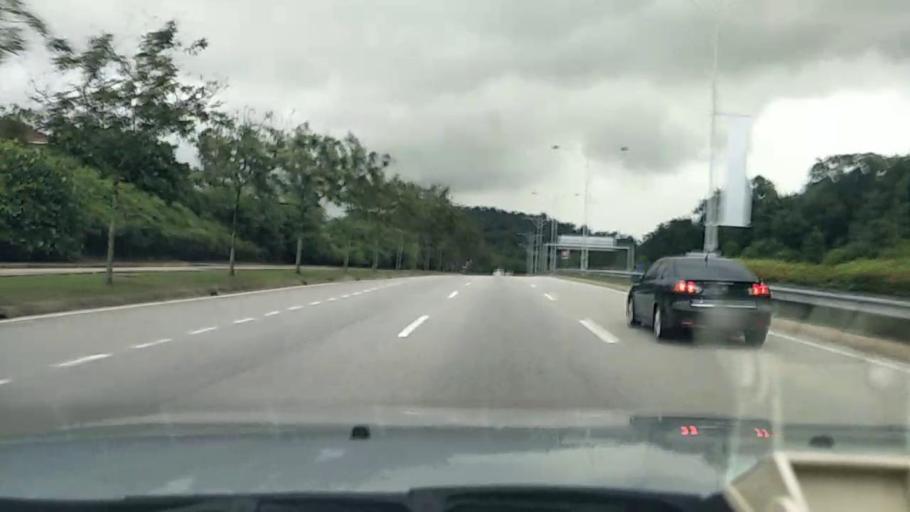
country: MY
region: Putrajaya
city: Putrajaya
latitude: 2.9457
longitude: 101.7136
